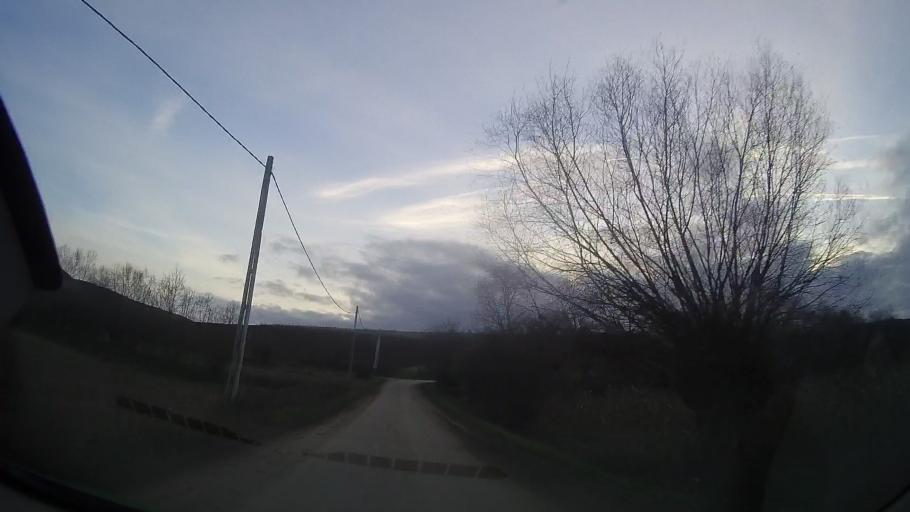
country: RO
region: Cluj
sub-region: Comuna Geaca
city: Geaca
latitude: 46.8521
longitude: 24.0552
